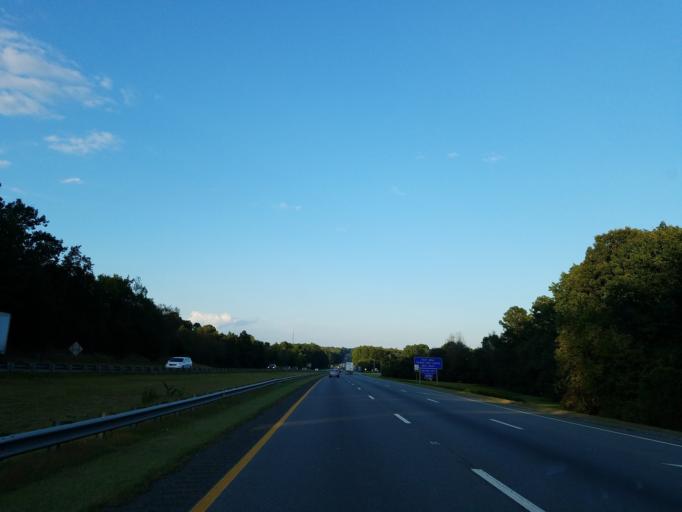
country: US
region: North Carolina
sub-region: Cleveland County
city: White Plains
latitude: 35.1816
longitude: -81.4110
